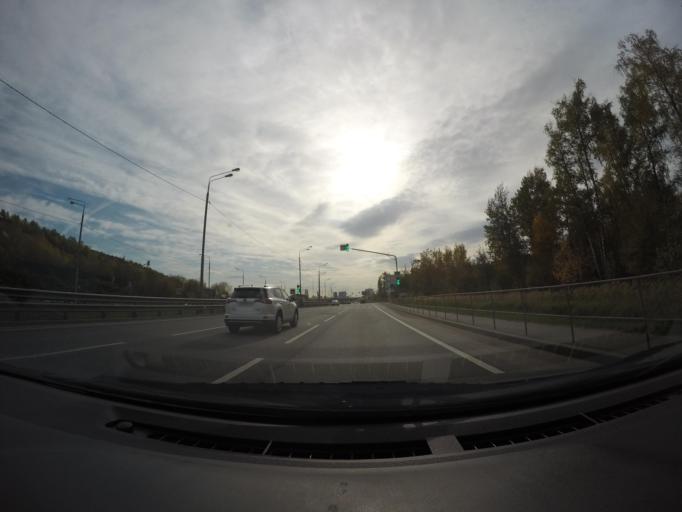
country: RU
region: Moscow
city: Businovo
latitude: 55.9052
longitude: 37.4925
